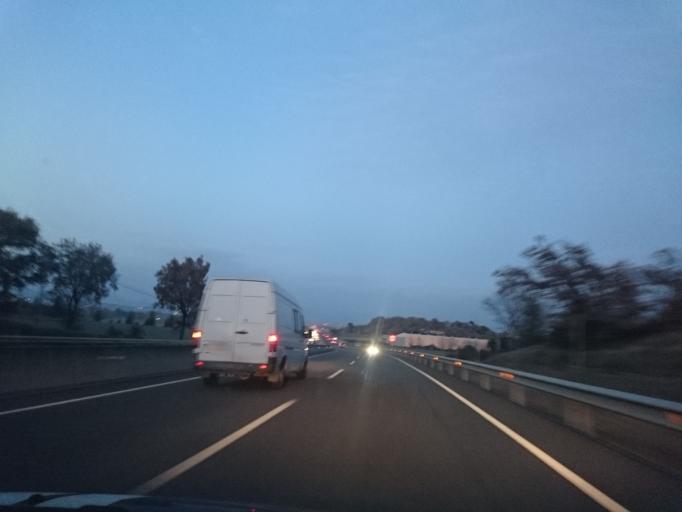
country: ES
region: Catalonia
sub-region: Provincia de Barcelona
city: Tona
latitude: 41.8847
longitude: 2.2427
